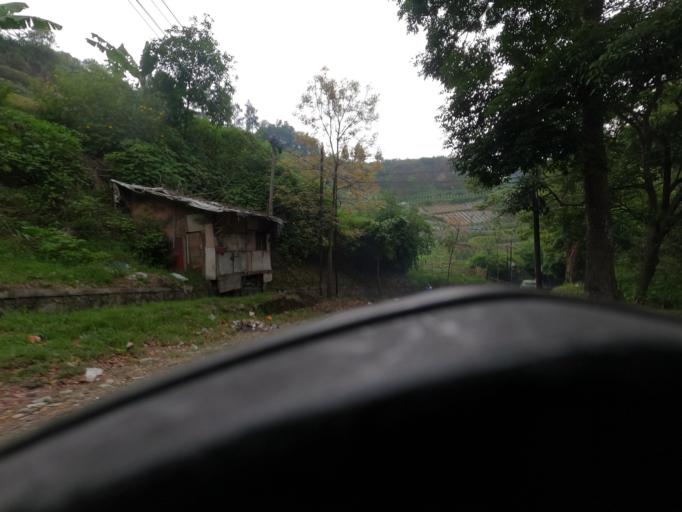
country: ID
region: West Java
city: Lembang
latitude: -6.8221
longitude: 107.6078
